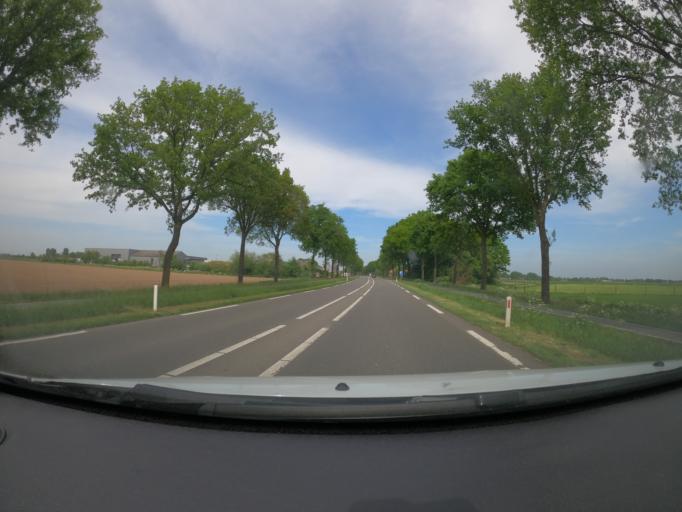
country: NL
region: Gelderland
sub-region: Gemeente Montferland
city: s-Heerenberg
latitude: 51.9023
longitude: 6.3124
